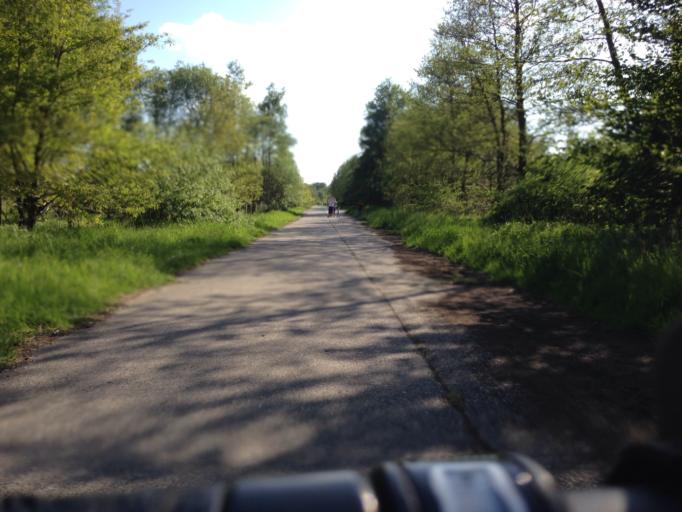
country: DE
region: Schleswig-Holstein
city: Stapelfeld
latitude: 53.6158
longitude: 10.1934
